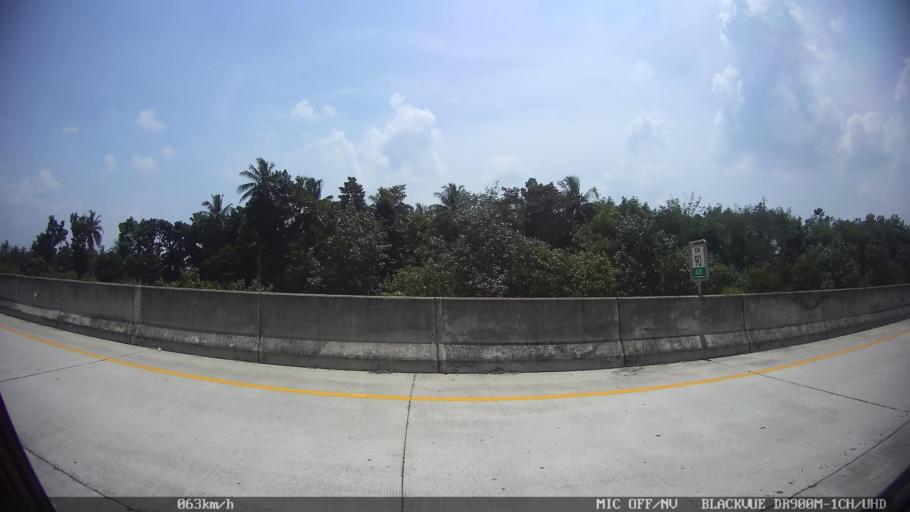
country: ID
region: Lampung
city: Natar
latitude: -5.3042
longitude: 105.2447
